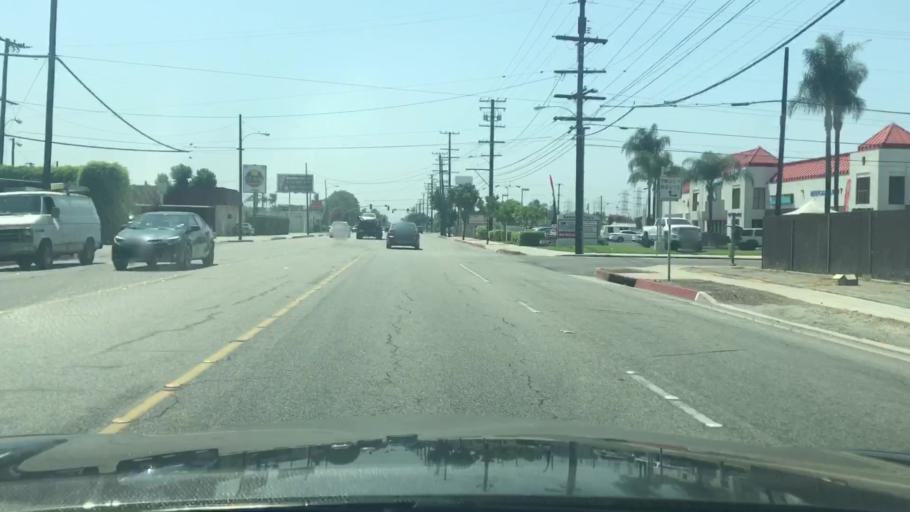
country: US
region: California
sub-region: Los Angeles County
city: Bellflower
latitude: 33.8752
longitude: -118.1173
